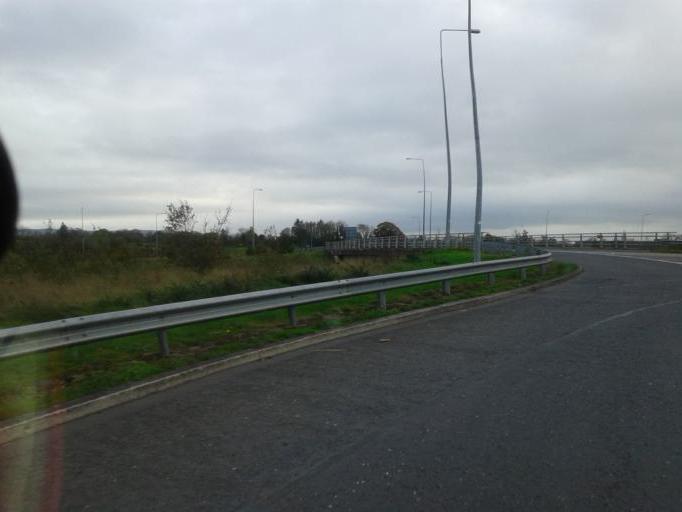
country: IE
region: Munster
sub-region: North Tipperary
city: Newport
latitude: 52.7573
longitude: -8.4093
